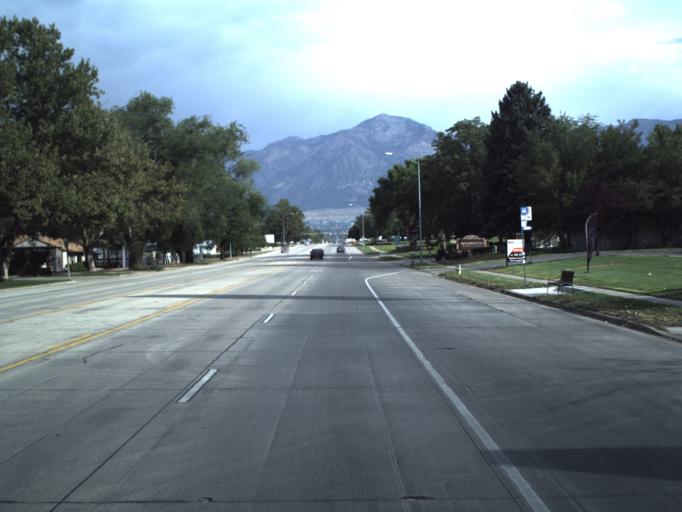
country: US
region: Utah
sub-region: Weber County
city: Harrisville
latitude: 41.2615
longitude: -111.9695
